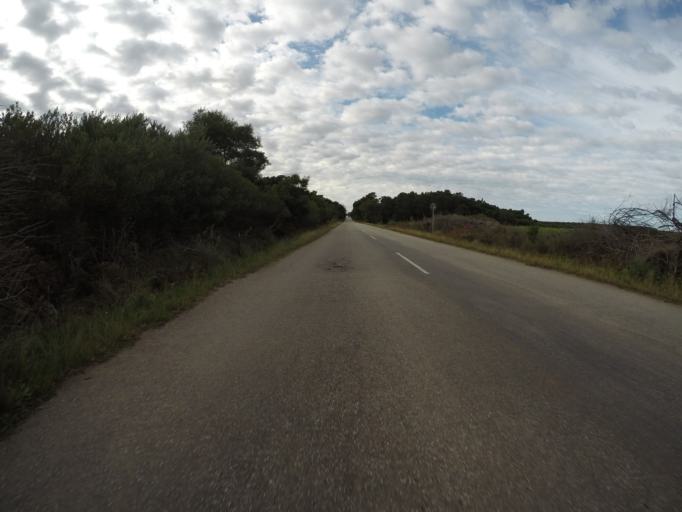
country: ZA
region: Eastern Cape
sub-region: Cacadu District Municipality
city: Kareedouw
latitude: -34.0225
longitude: 24.3601
